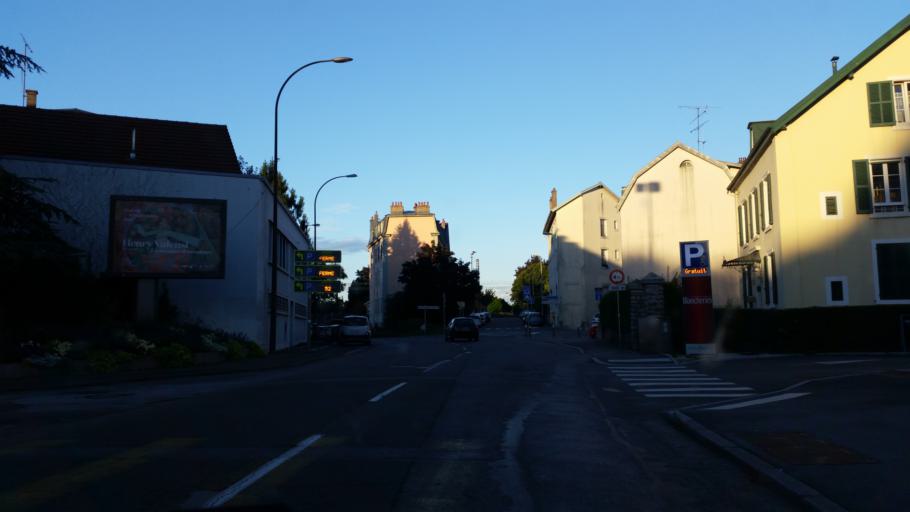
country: FR
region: Franche-Comte
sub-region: Departement du Doubs
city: Montbeliard
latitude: 47.5082
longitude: 6.8012
